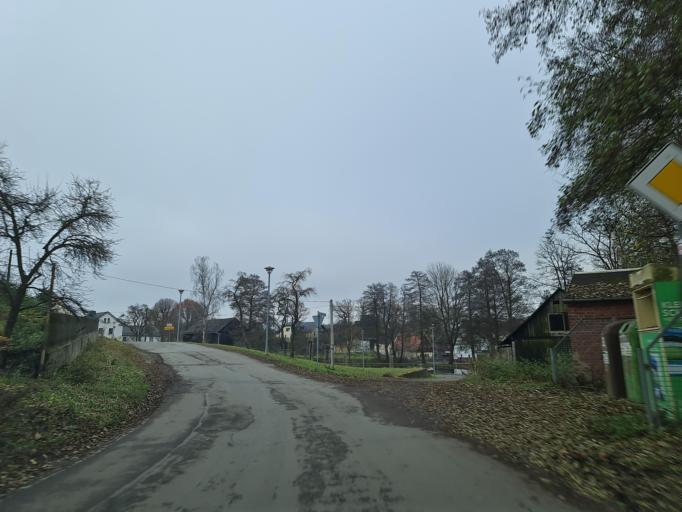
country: DE
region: Saxony
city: Syrau
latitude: 50.5115
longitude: 12.0890
